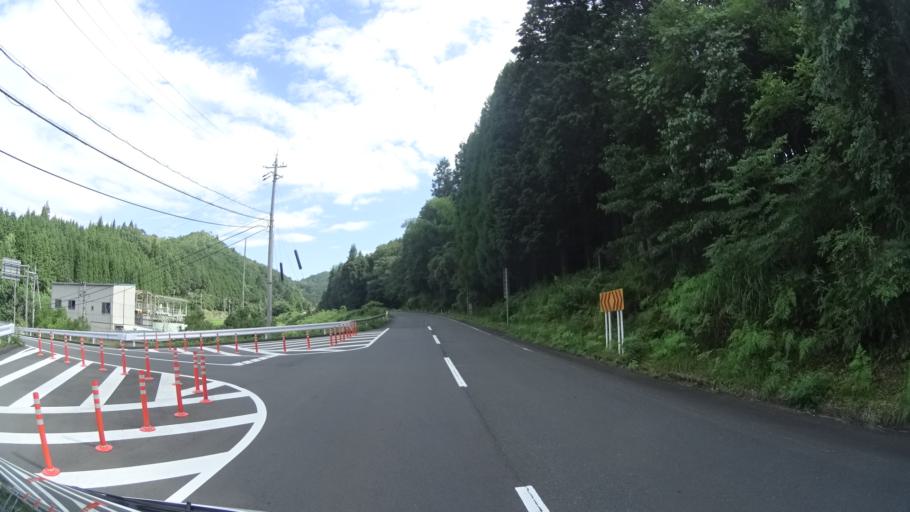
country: JP
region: Kyoto
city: Fukuchiyama
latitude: 35.3546
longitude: 135.1492
